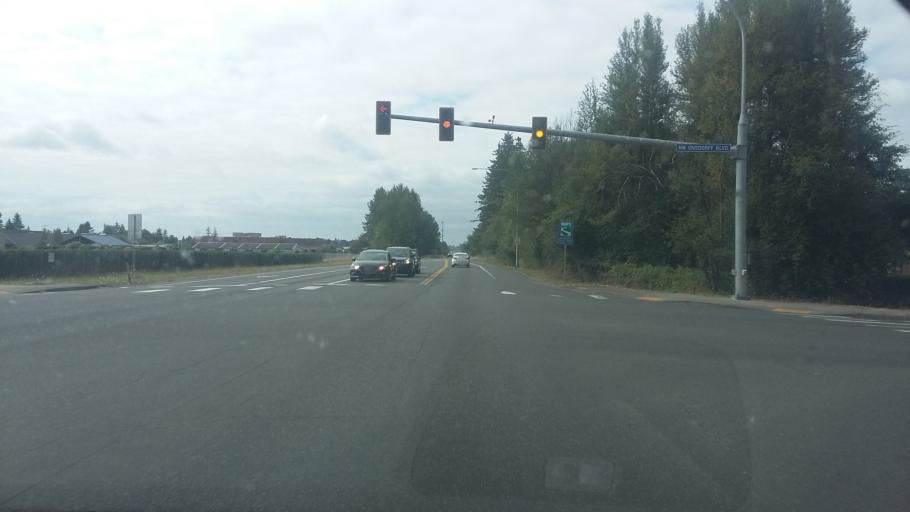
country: US
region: Washington
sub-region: Clark County
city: Battle Ground
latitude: 45.7919
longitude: -122.5475
